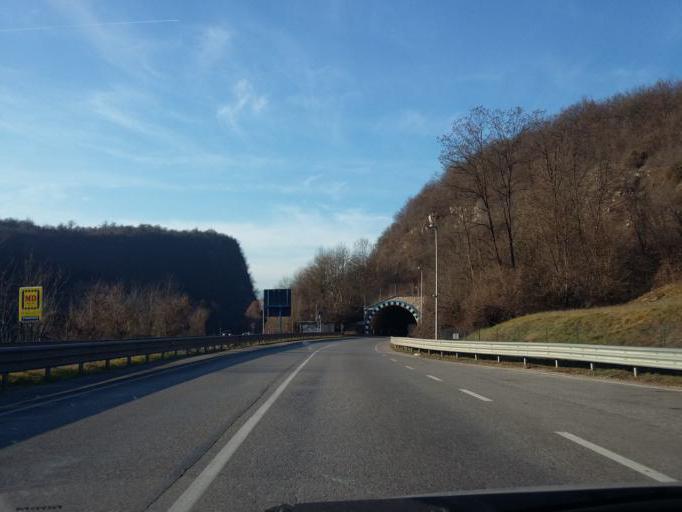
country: IT
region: Lombardy
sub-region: Provincia di Brescia
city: Sabbio Chiese
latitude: 45.6469
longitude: 10.4528
